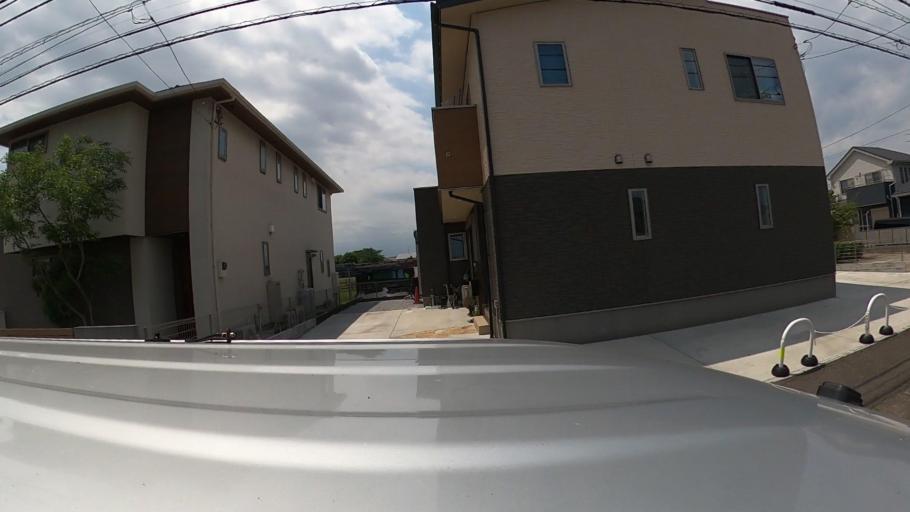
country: JP
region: Kanagawa
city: Chigasaki
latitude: 35.3815
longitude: 139.4013
